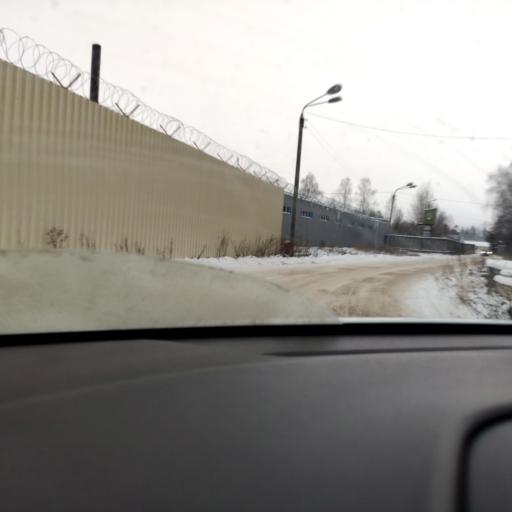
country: RU
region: Tatarstan
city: Osinovo
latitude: 55.8908
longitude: 48.8271
